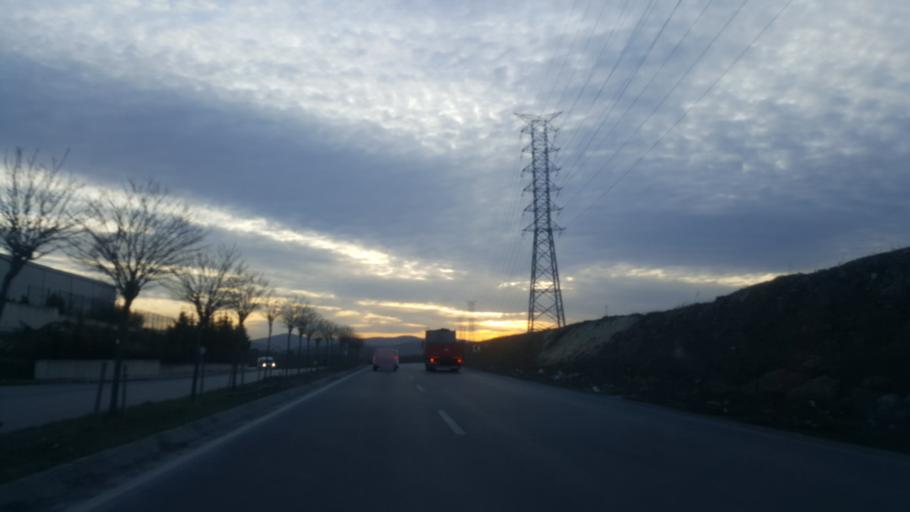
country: TR
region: Kocaeli
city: Tavsancil
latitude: 40.8085
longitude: 29.5634
